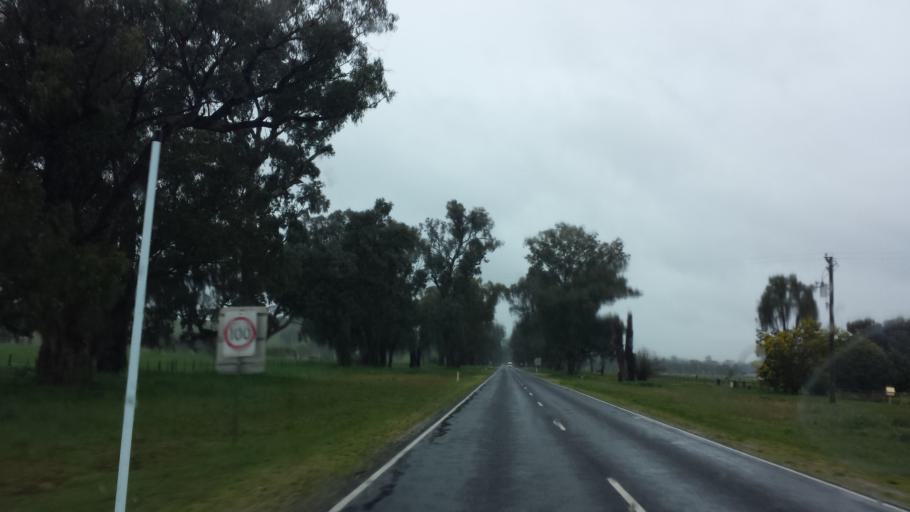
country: AU
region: Victoria
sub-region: Wangaratta
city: Wangaratta
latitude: -36.4388
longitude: 146.5460
